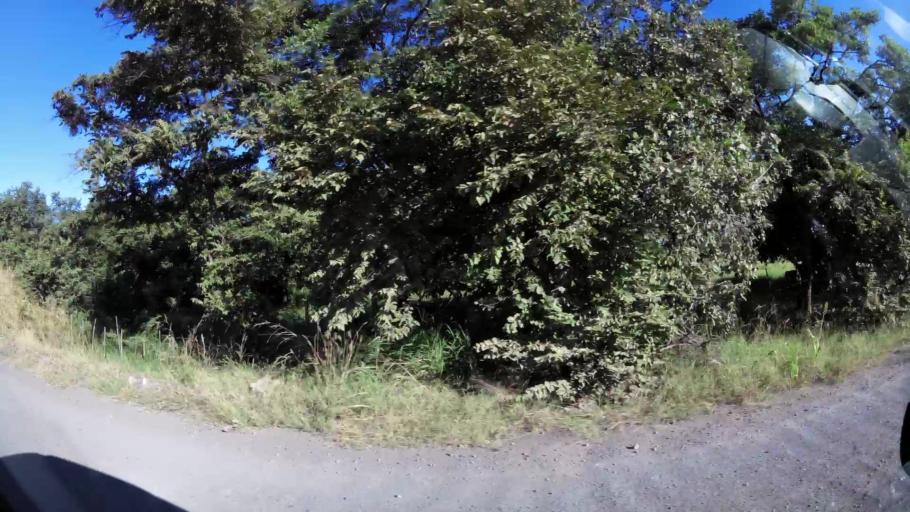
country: CR
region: Guanacaste
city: Belen
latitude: 10.4857
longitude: -85.5731
